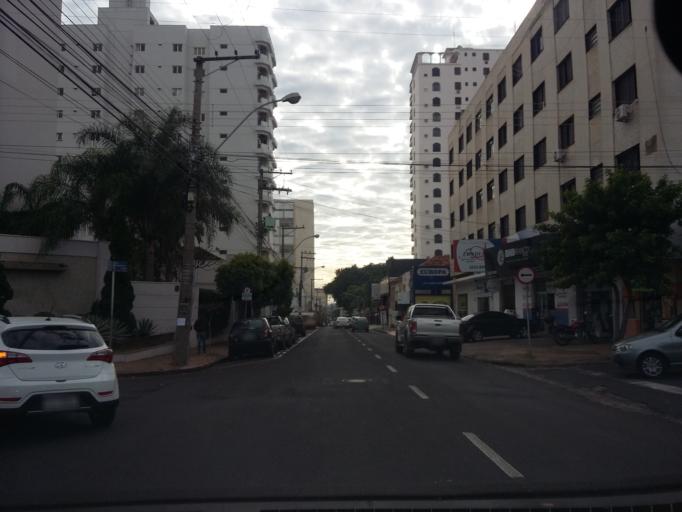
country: BR
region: Sao Paulo
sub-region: Sao Jose Do Rio Preto
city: Sao Jose do Rio Preto
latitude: -20.8173
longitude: -49.3870
